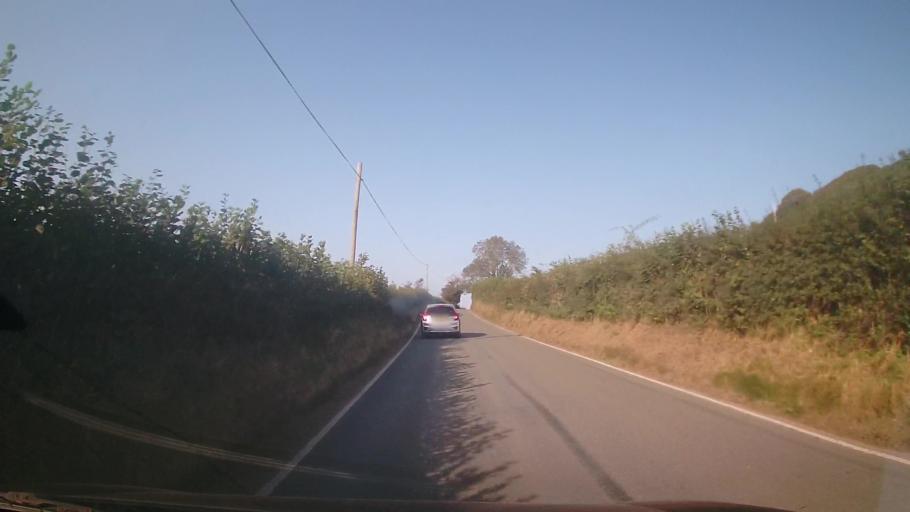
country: GB
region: Wales
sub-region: County of Ceredigion
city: Lledrod
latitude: 52.2348
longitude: -3.9291
